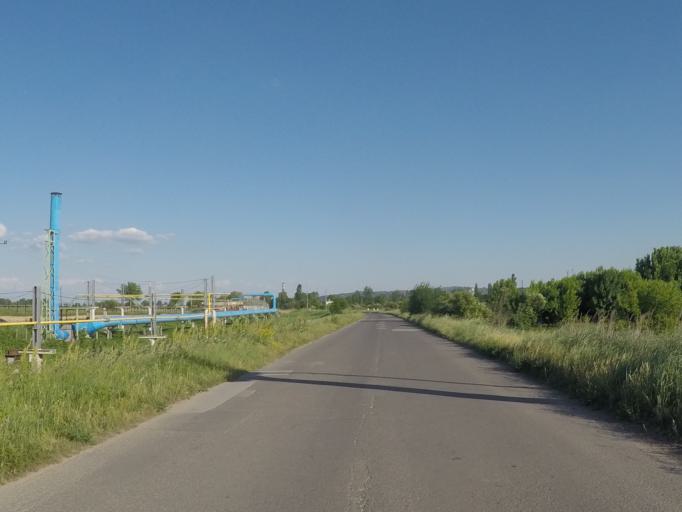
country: HU
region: Borsod-Abauj-Zemplen
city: Kazincbarcika
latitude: 48.2502
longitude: 20.6607
